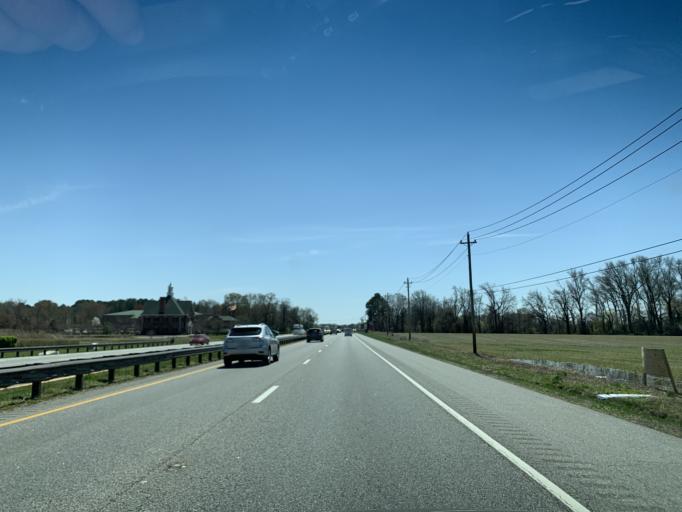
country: US
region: Maryland
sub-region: Talbot County
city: Easton
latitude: 38.7887
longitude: -76.0603
